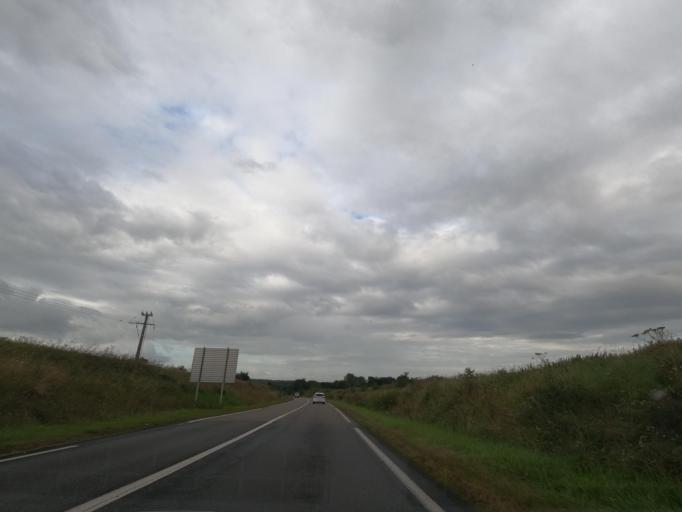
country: FR
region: Haute-Normandie
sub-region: Departement de l'Eure
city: Bourgtheroulde-Infreville
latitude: 49.2934
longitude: 0.8794
